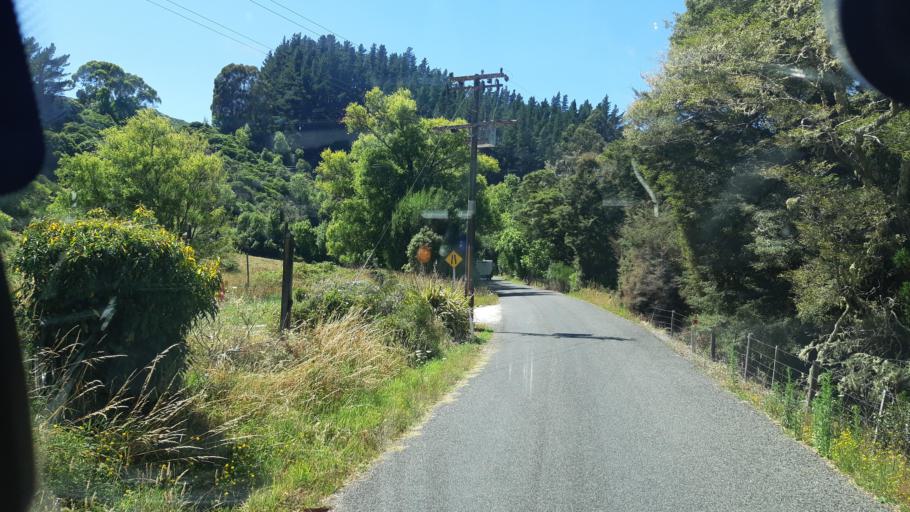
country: NZ
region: Tasman
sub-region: Tasman District
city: Motueka
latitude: -41.0360
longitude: 172.9065
